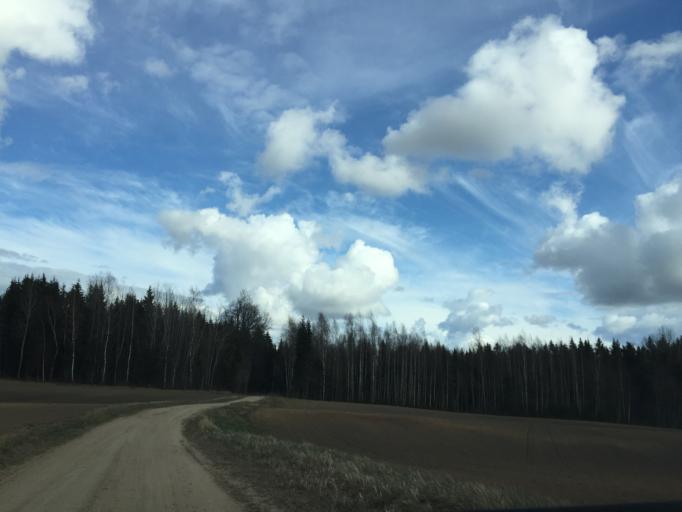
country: LV
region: Burtnieki
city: Matisi
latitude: 57.6169
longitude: 24.9996
